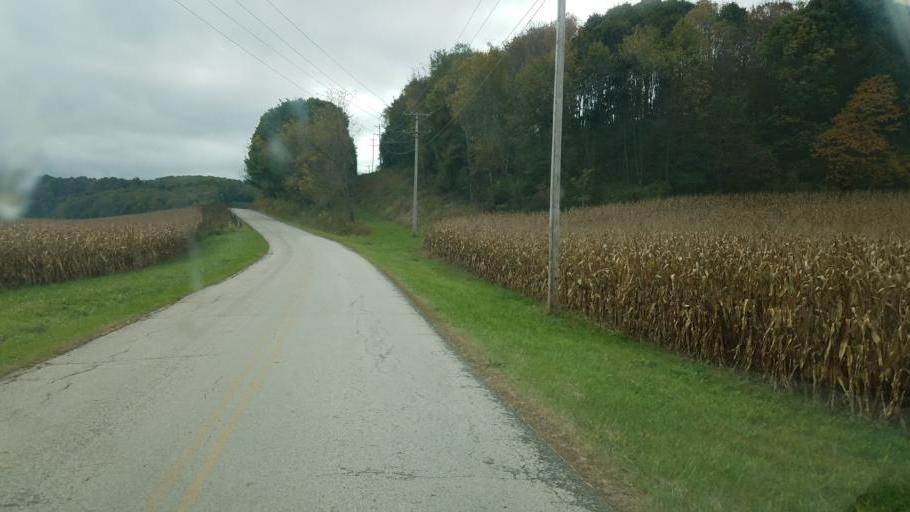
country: US
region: Ohio
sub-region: Ashland County
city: Loudonville
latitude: 40.5912
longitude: -82.1681
